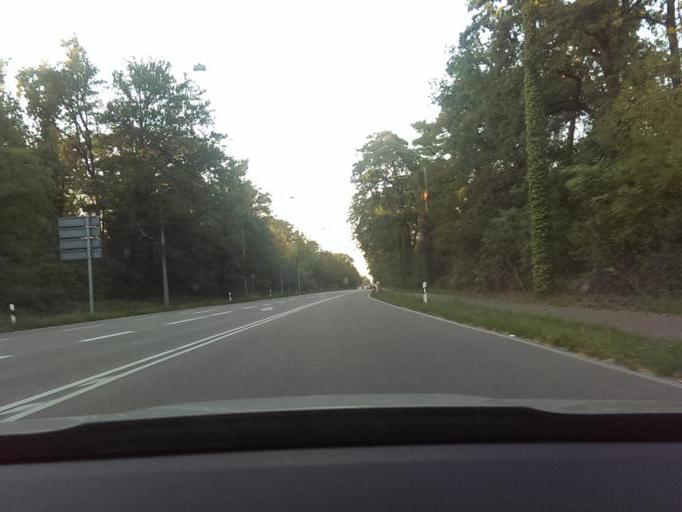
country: DE
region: Baden-Wuerttemberg
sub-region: Karlsruhe Region
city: Karlsruhe
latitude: 49.0243
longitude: 8.3967
